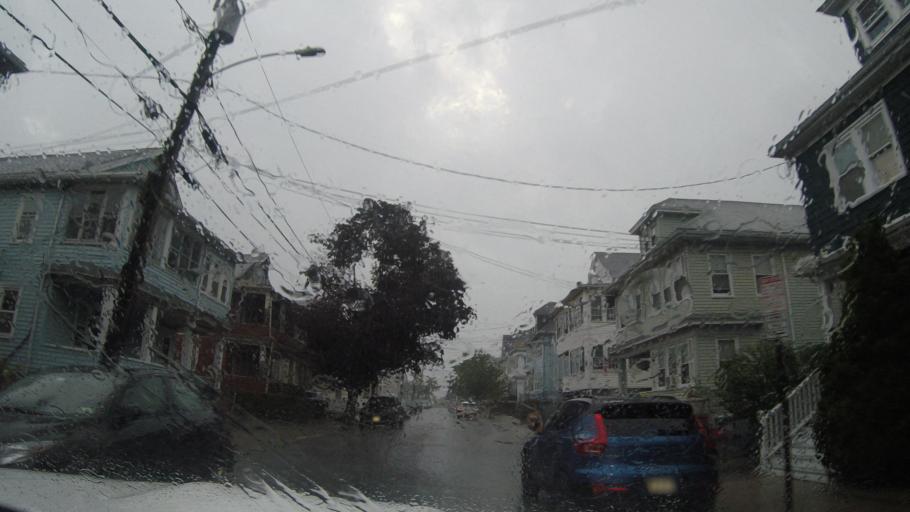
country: US
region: Massachusetts
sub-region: Middlesex County
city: Somerville
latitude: 42.3955
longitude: -71.0867
